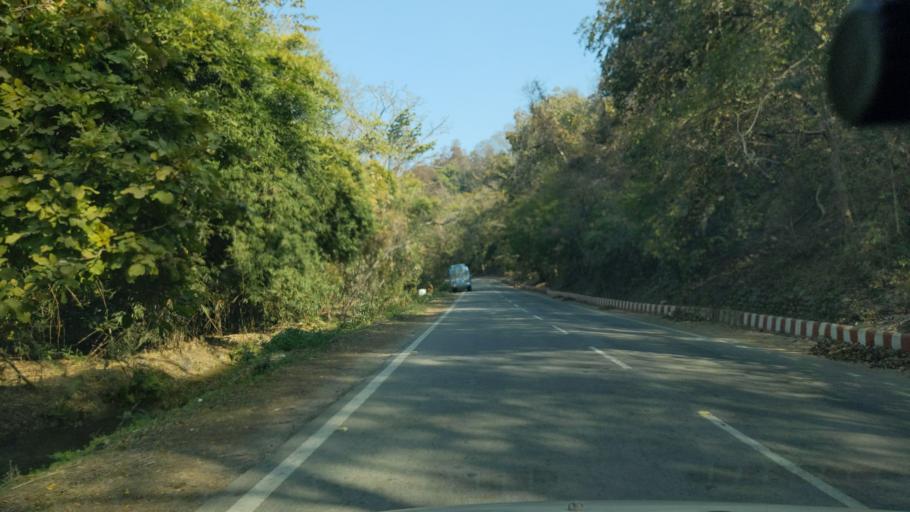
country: IN
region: Uttarakhand
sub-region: Naini Tal
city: Ramnagar
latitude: 29.3916
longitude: 79.1378
